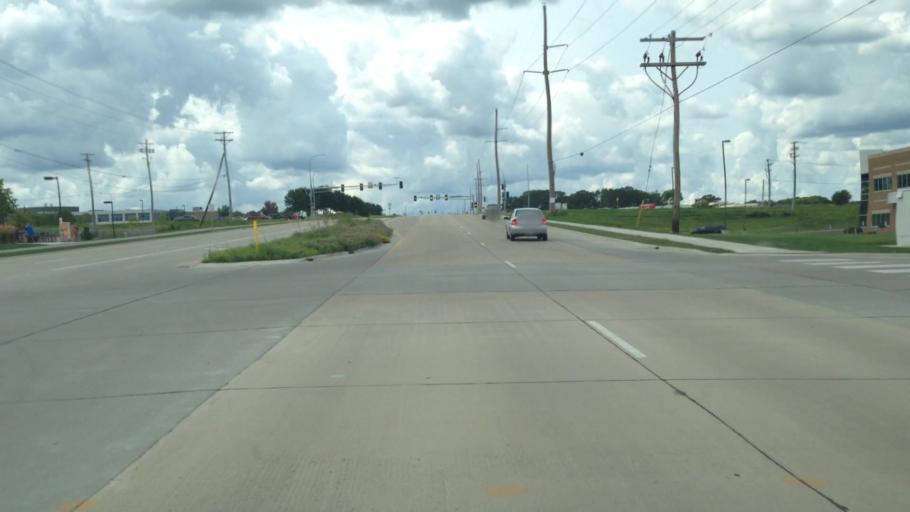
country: US
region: Minnesota
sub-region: Olmsted County
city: Rochester
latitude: 44.0580
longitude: -92.5213
